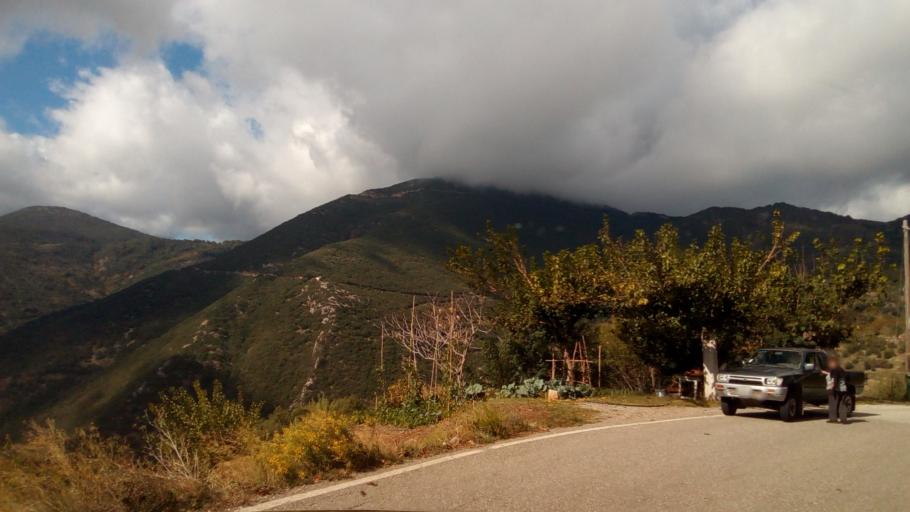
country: GR
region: West Greece
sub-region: Nomos Aitolias kai Akarnanias
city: Nafpaktos
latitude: 38.4858
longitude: 21.8527
